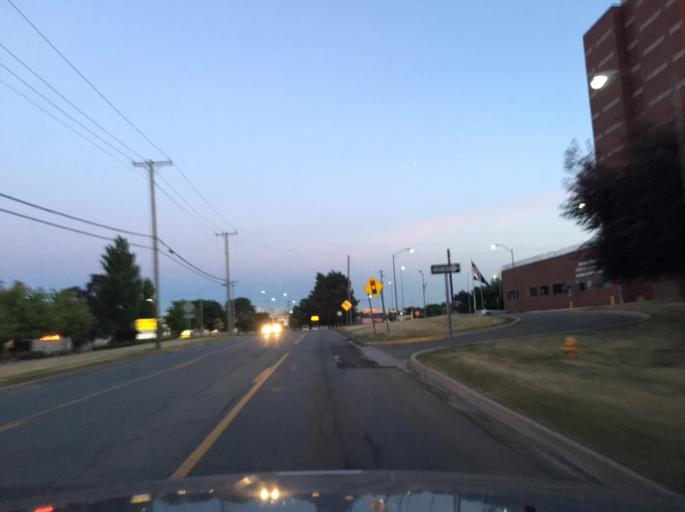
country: US
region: Michigan
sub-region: Macomb County
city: Mount Clemens
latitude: 42.6176
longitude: -82.8877
